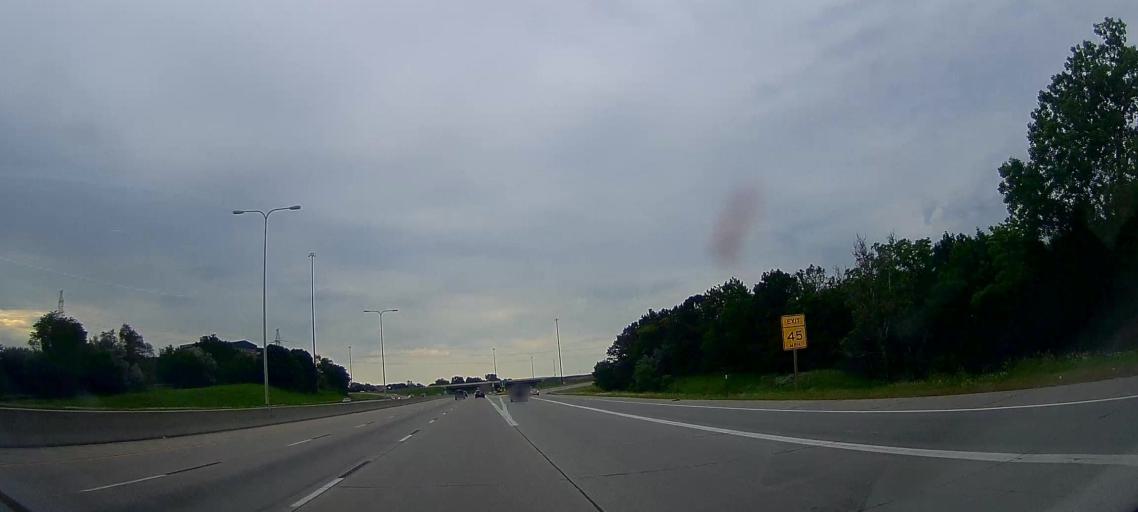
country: US
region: Nebraska
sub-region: Douglas County
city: Ralston
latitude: 41.2814
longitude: -96.0759
